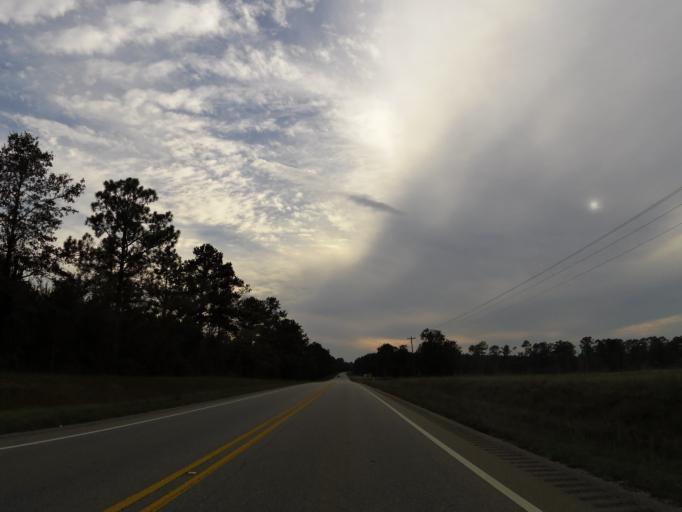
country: US
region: Alabama
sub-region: Monroe County
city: Frisco City
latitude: 31.3219
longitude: -87.4674
